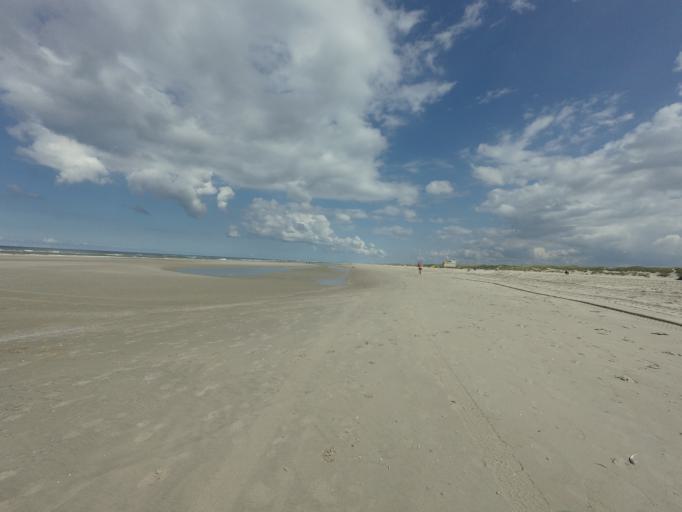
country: NL
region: Friesland
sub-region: Gemeente Terschelling
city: West-Terschelling
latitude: 53.4035
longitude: 5.2472
